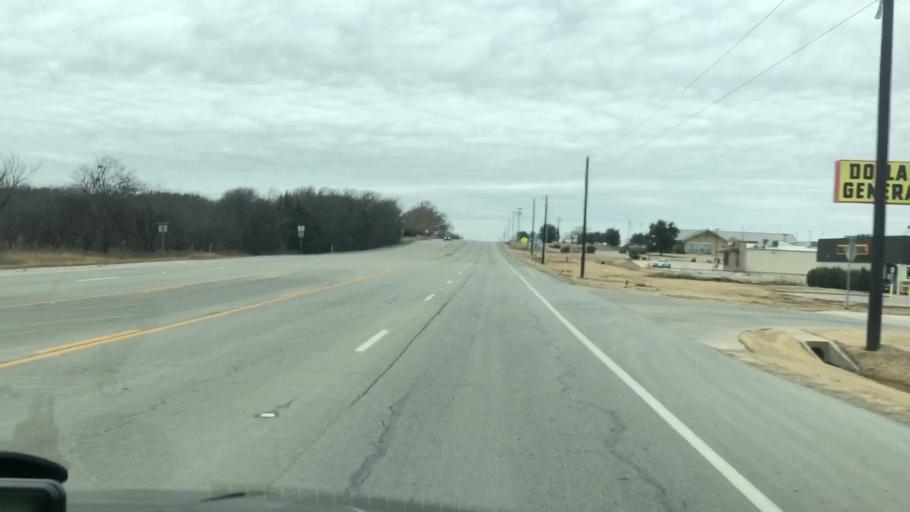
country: US
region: Texas
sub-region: Jack County
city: Jacksboro
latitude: 33.2275
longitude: -98.1648
